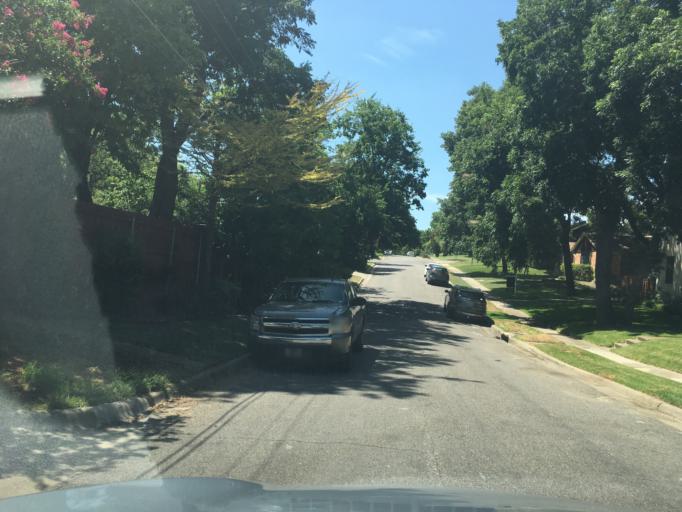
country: US
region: Texas
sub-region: Dallas County
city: Highland Park
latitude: 32.8635
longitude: -96.7277
